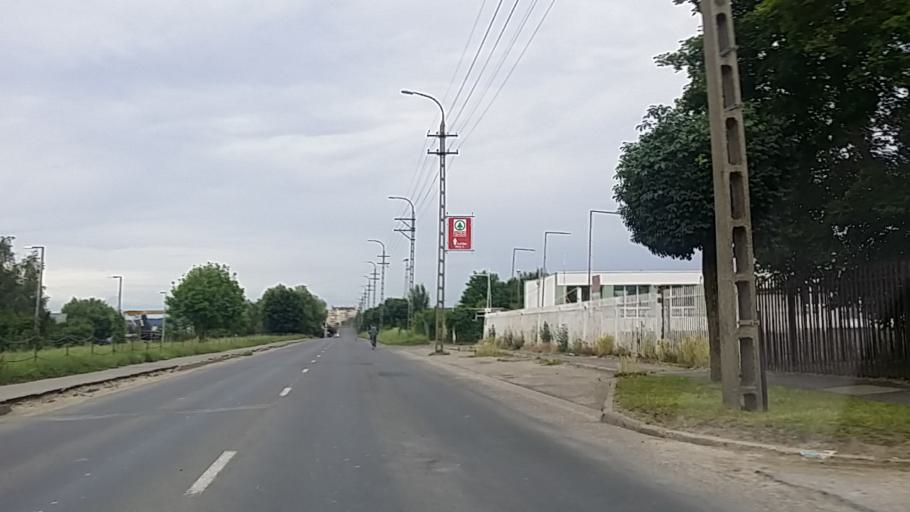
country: HU
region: Zala
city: Zalaegerszeg
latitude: 46.8520
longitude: 16.8149
